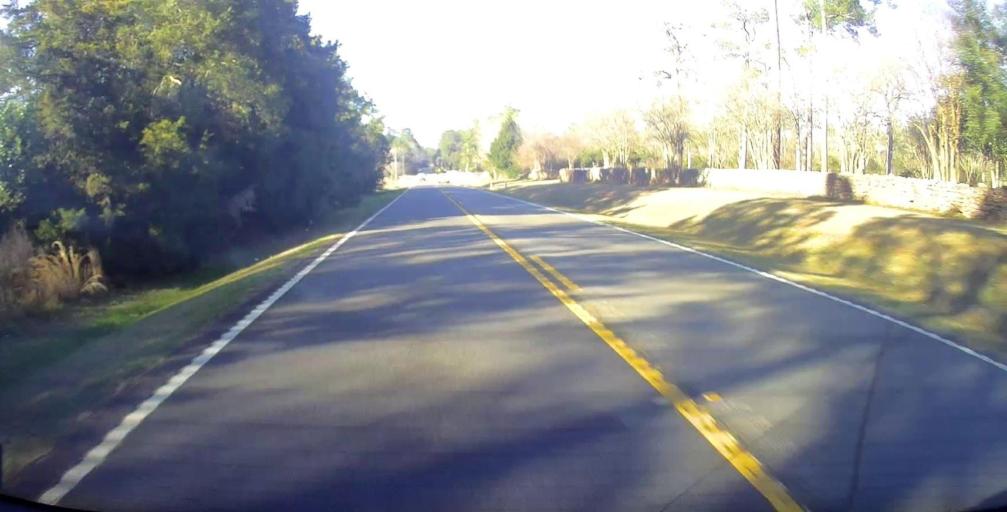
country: US
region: Georgia
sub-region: Sumter County
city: Americus
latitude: 32.0204
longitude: -84.2192
